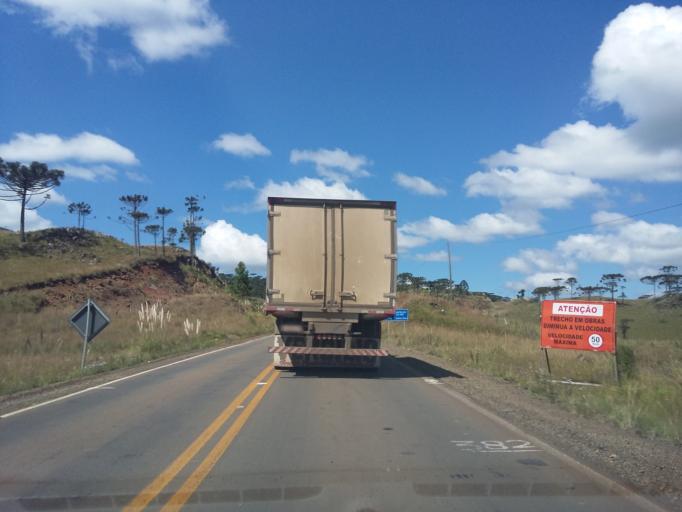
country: BR
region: Santa Catarina
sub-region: Sao Joaquim
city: Sao Joaquim
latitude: -28.3154
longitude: -49.7125
